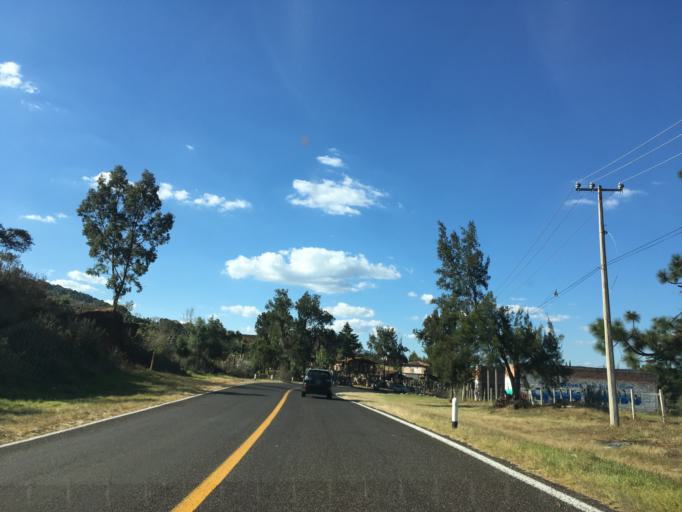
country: MX
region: Michoacan
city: Tzintzuntzan
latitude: 19.6200
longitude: -101.5768
